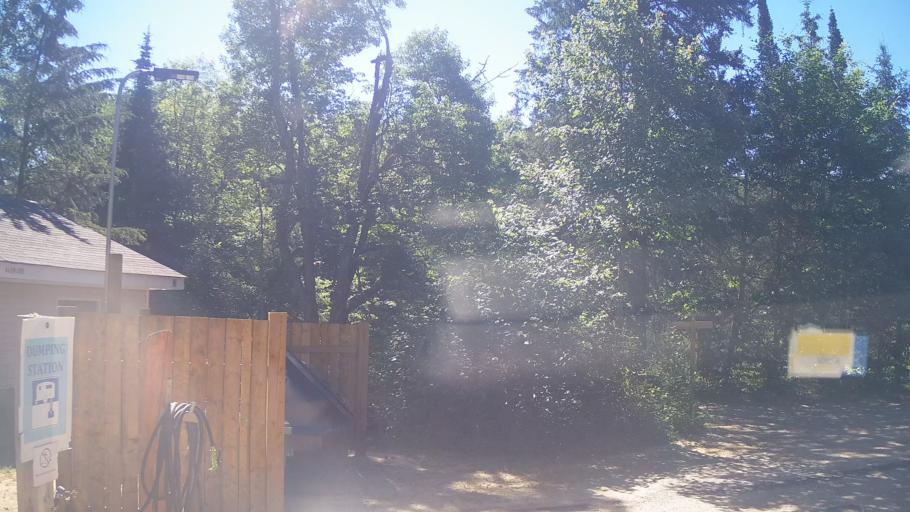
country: CA
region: Ontario
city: Huntsville
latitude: 45.3772
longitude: -79.2149
